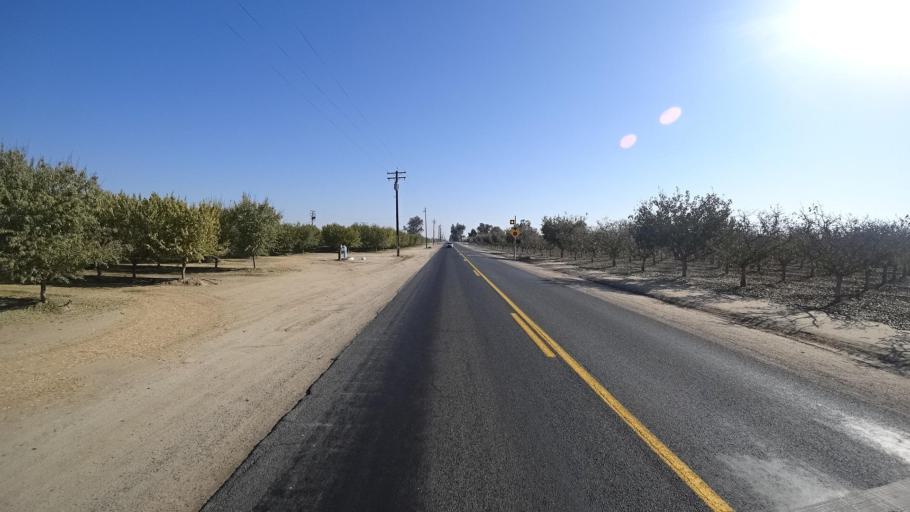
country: US
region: California
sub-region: Kern County
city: Delano
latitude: 35.7177
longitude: -119.3337
